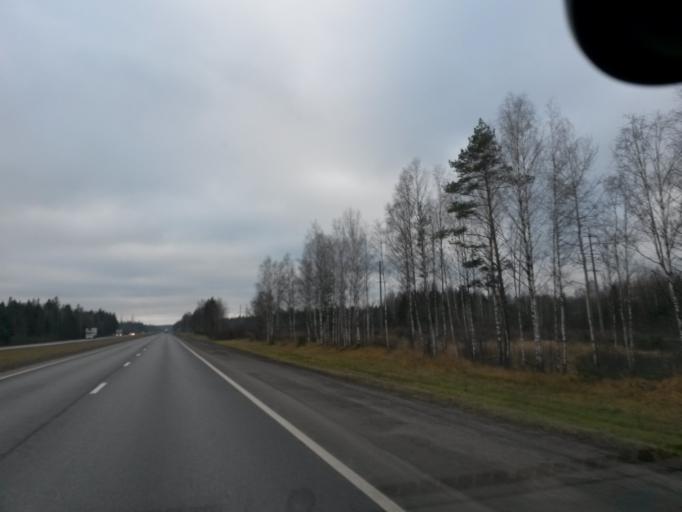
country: RU
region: Jaroslavl
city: Krasnyye Tkachi
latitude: 57.4849
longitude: 39.7751
